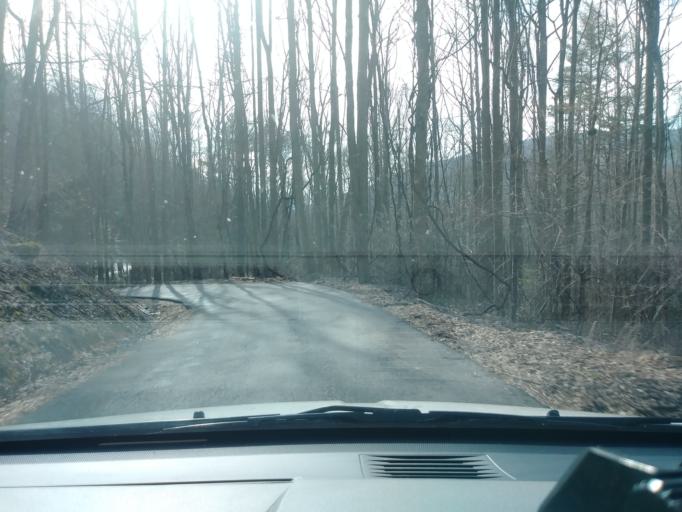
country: US
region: Tennessee
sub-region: Greene County
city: Tusculum
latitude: 36.0226
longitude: -82.7347
